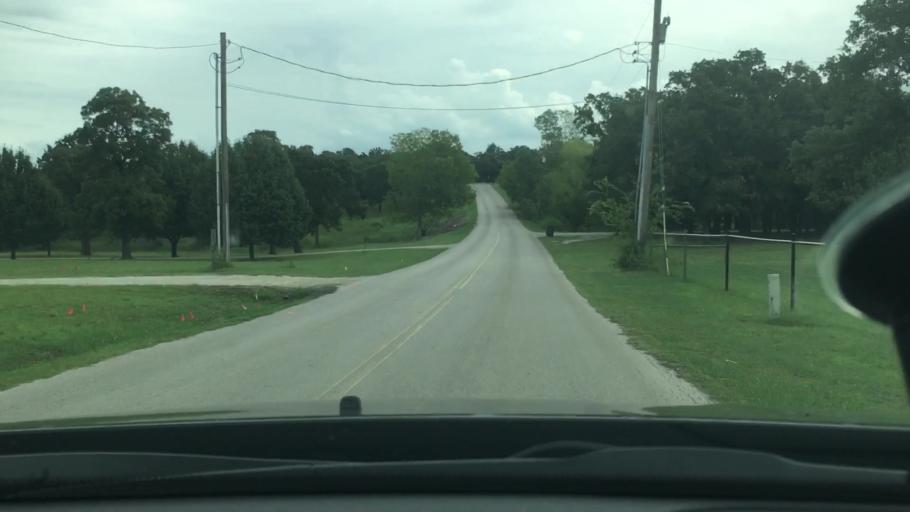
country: US
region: Oklahoma
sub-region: Carter County
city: Healdton
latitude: 34.2164
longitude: -97.4837
